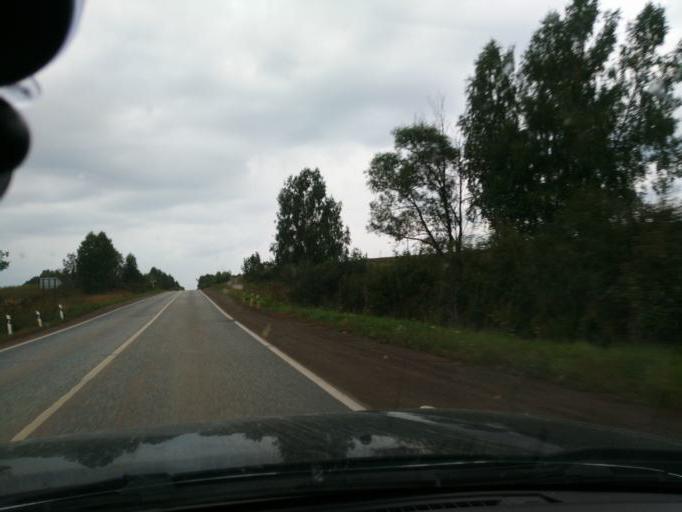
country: RU
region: Perm
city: Chernushka
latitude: 56.8428
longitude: 55.9780
